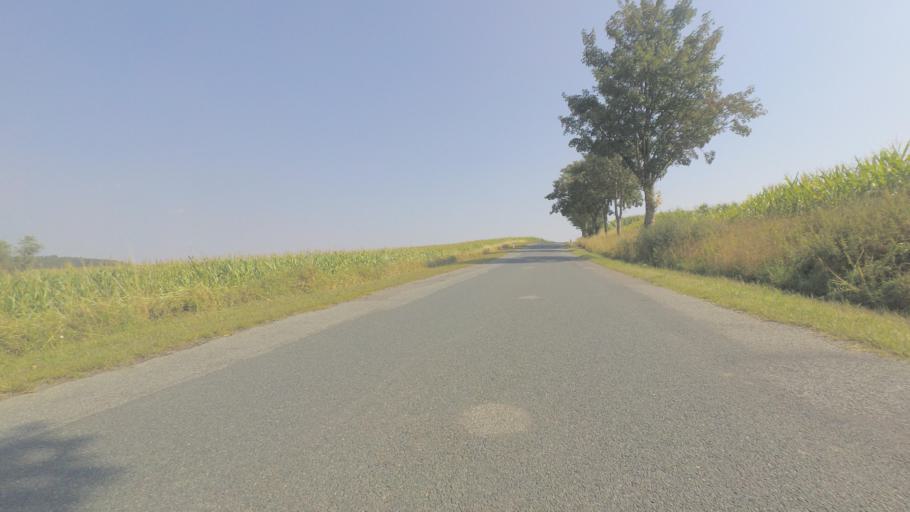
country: DE
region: Mecklenburg-Vorpommern
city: Pampow
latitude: 53.7038
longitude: 12.6105
